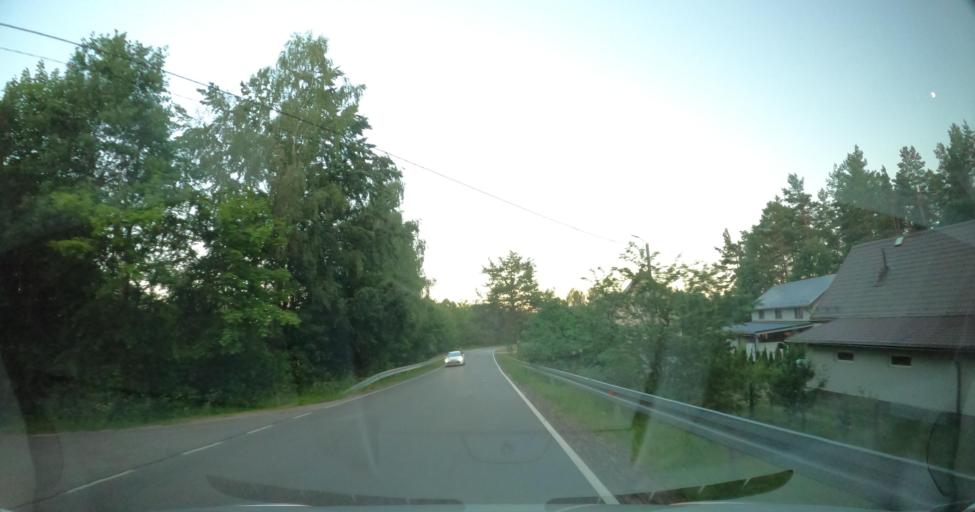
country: PL
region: Pomeranian Voivodeship
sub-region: Powiat wejherowski
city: Leczyce
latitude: 54.4990
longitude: 17.8404
